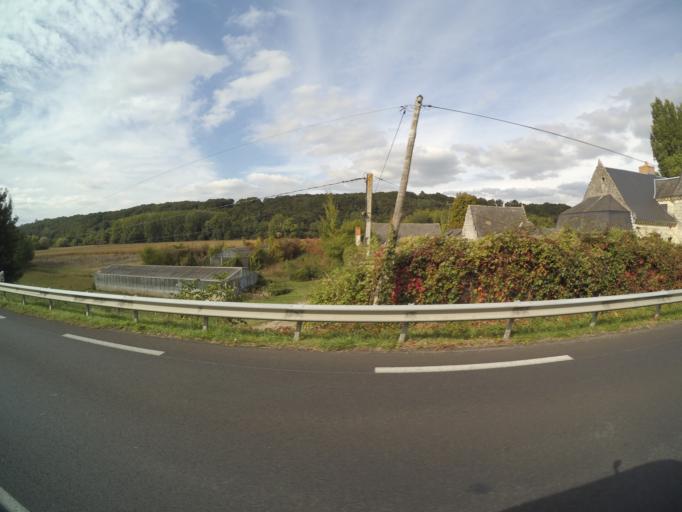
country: FR
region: Centre
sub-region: Departement d'Indre-et-Loire
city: Langeais
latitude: 47.2926
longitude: 0.3344
